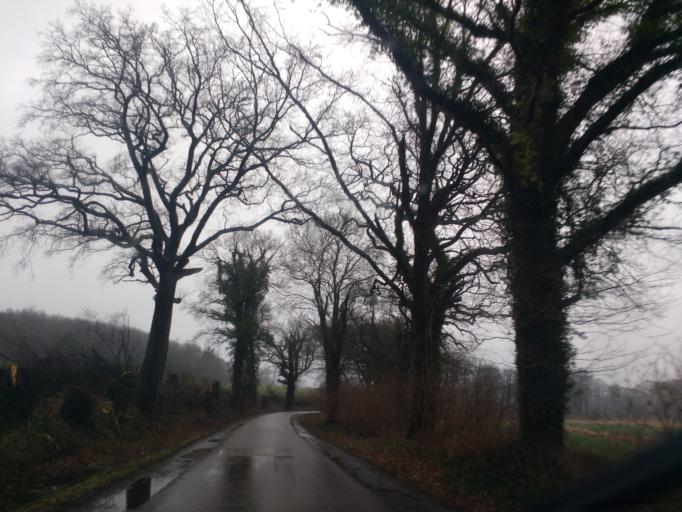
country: DE
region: Schleswig-Holstein
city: Wangels
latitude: 54.3010
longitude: 10.7503
